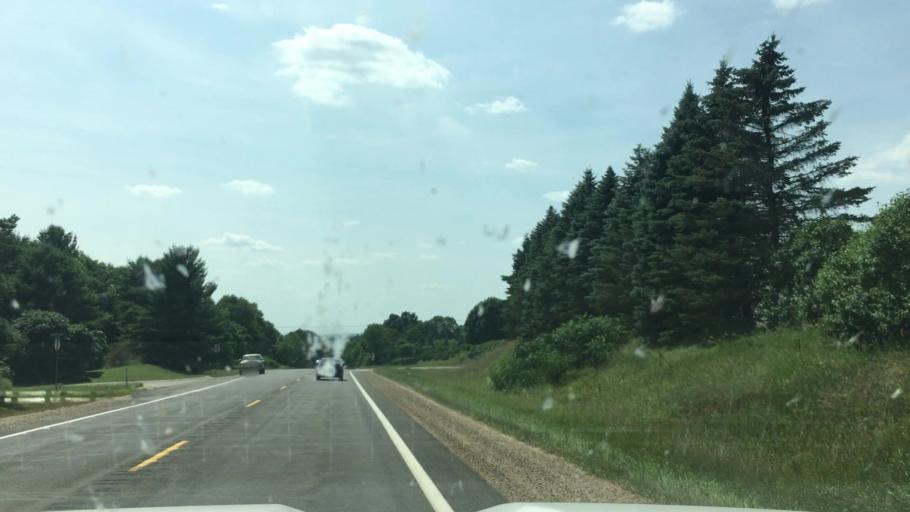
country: US
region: Michigan
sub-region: Allegan County
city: Plainwell
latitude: 42.4432
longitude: -85.6007
